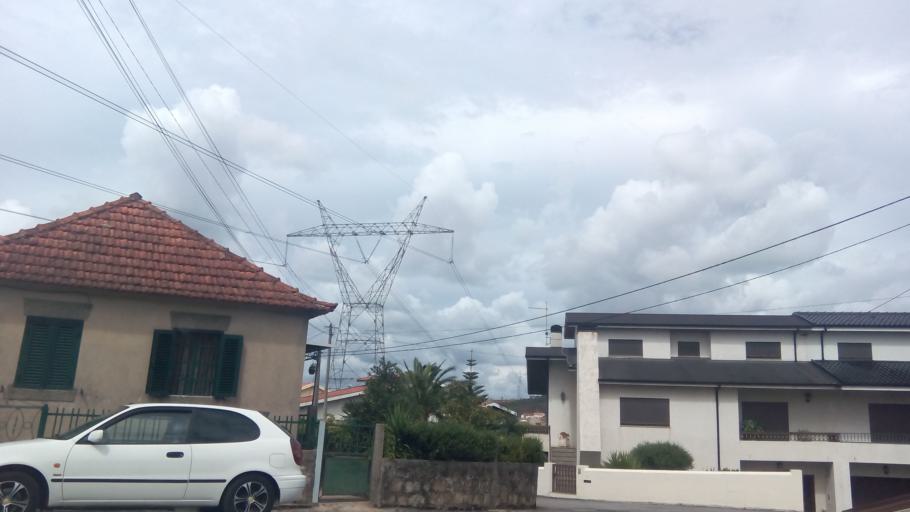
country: PT
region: Porto
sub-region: Paredes
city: Gandra
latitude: 41.1934
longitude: -8.4383
